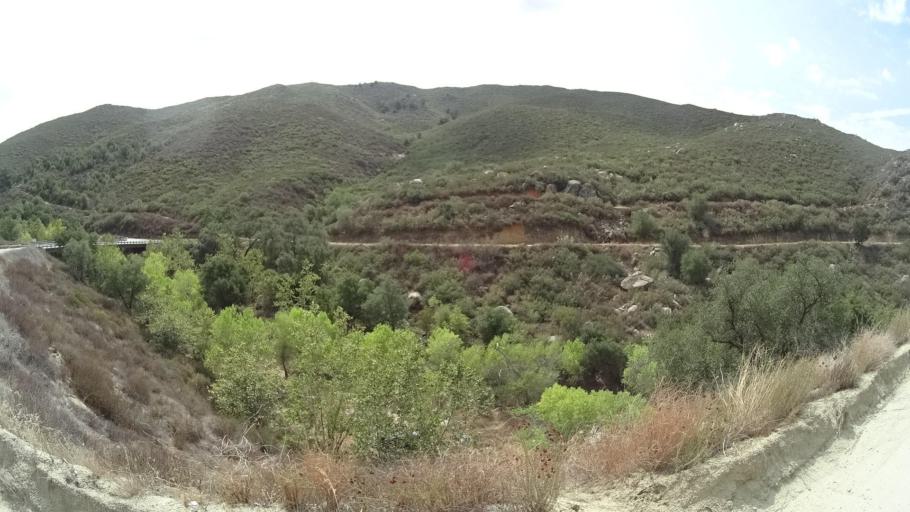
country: US
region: California
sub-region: San Diego County
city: Ramona
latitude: 33.1242
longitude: -116.8014
